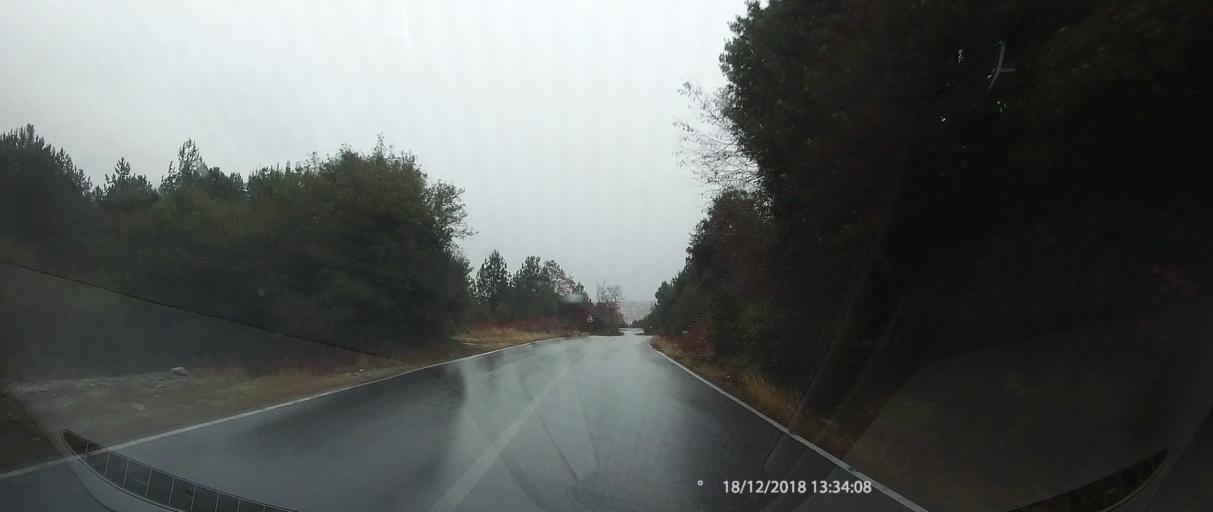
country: GR
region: Central Macedonia
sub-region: Nomos Pierias
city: Litochoro
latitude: 40.1141
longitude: 22.4840
